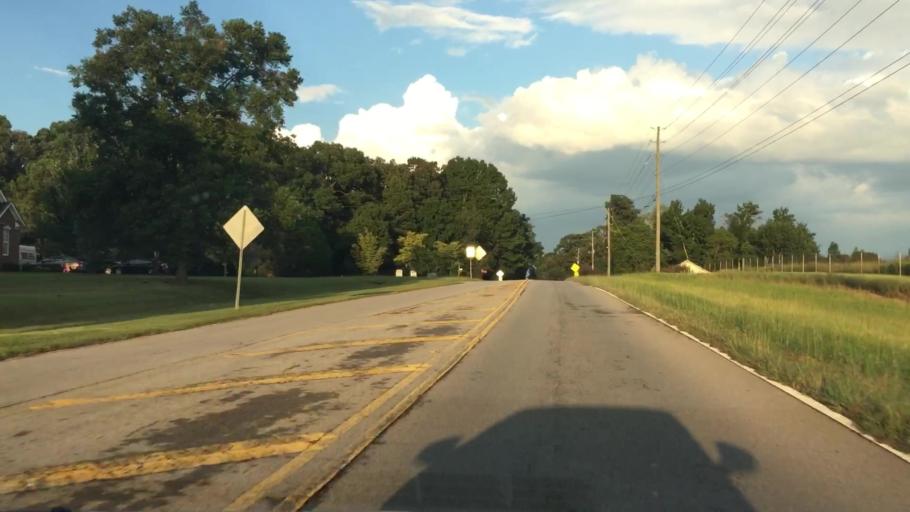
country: US
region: Georgia
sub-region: Henry County
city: McDonough
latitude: 33.4913
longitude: -84.1668
